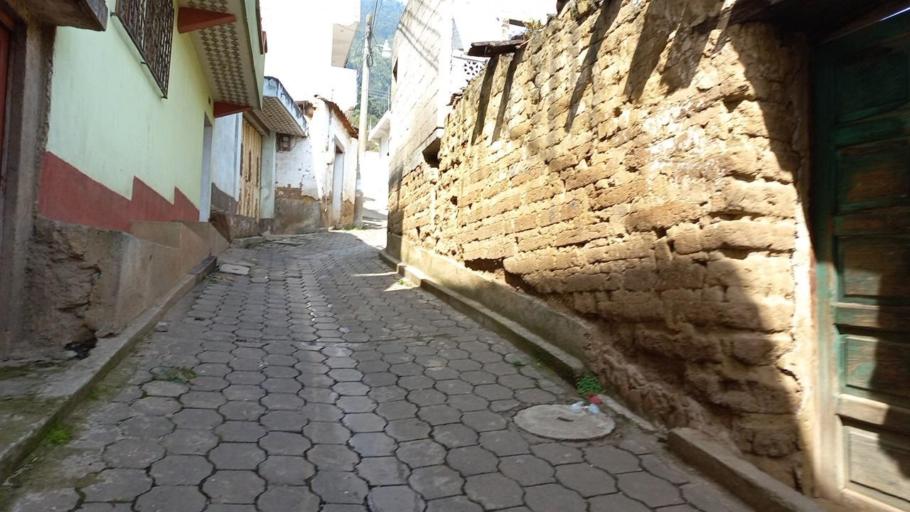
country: GT
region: Totonicapan
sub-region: Municipio de San Andres Xecul
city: San Andres Xecul
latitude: 14.9032
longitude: -91.4837
